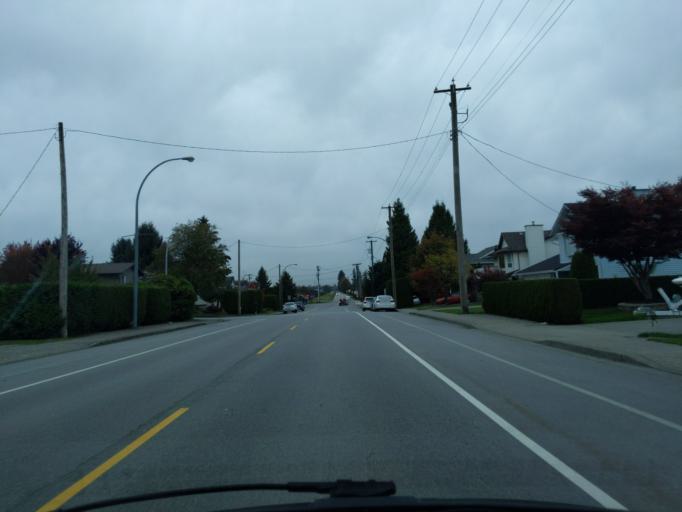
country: CA
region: British Columbia
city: Pitt Meadows
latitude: 49.2224
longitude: -122.6986
